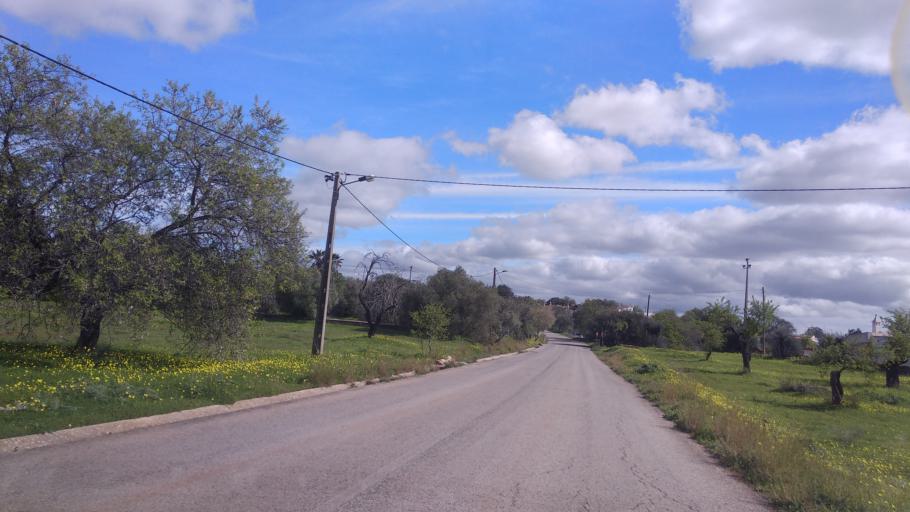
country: PT
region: Faro
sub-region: Sao Bras de Alportel
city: Sao Bras de Alportel
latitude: 37.1499
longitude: -7.9158
